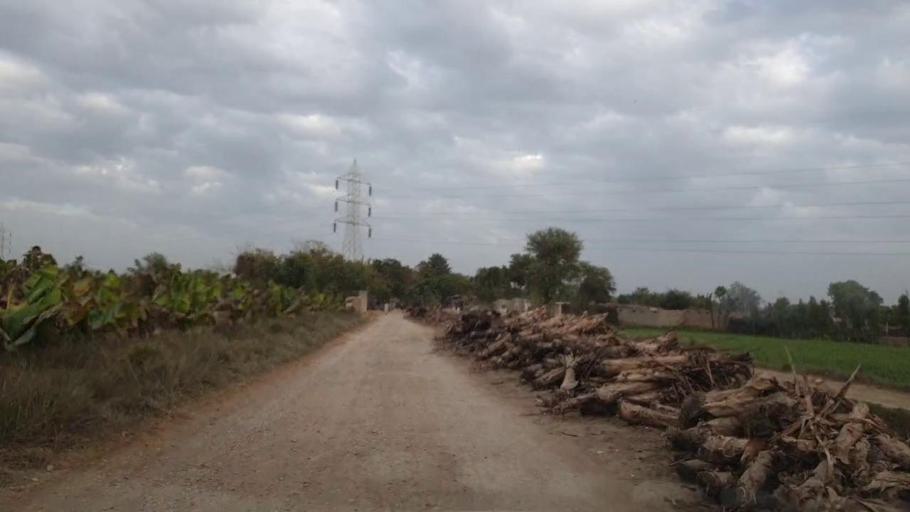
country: PK
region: Sindh
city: Matiari
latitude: 25.6242
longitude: 68.4870
